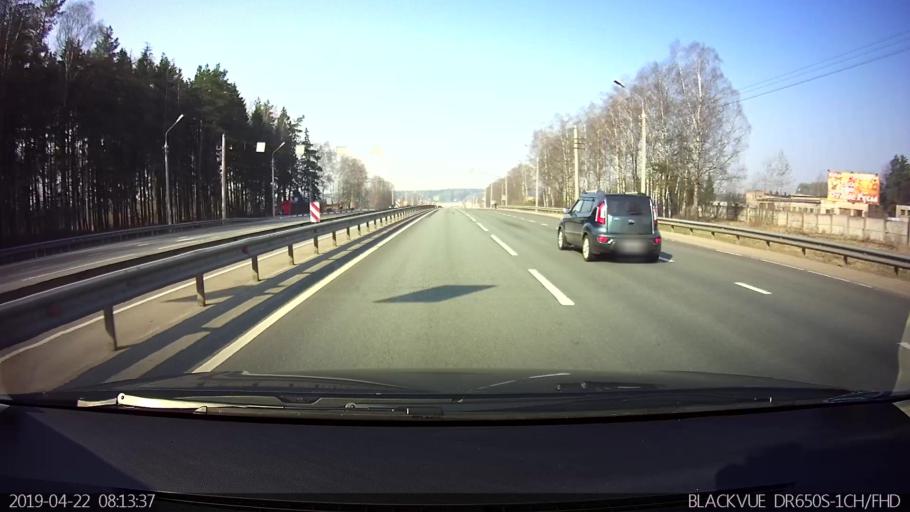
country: RU
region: Smolensk
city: Yartsevo
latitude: 55.0818
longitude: 32.7627
